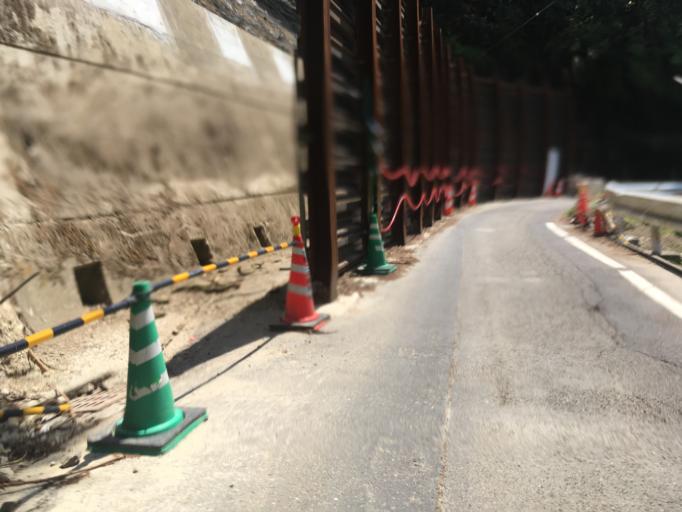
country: JP
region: Kyoto
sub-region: Kyoto-shi
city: Kamigyo-ku
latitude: 35.1046
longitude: 135.7395
